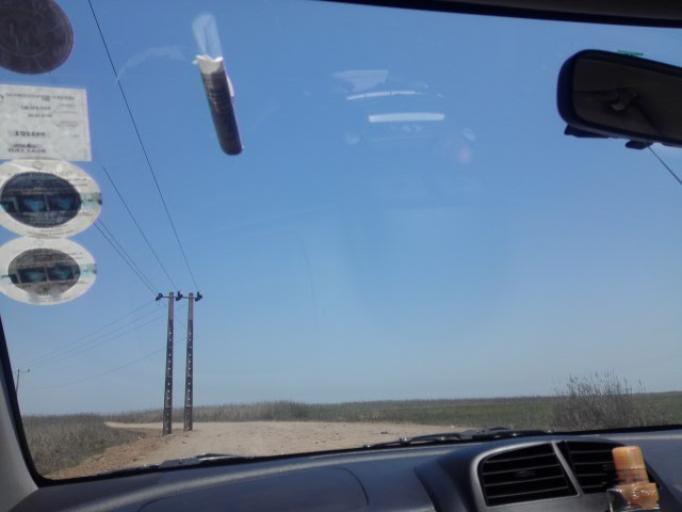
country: MZ
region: Maputo City
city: Maputo
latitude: -25.7327
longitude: 32.7209
